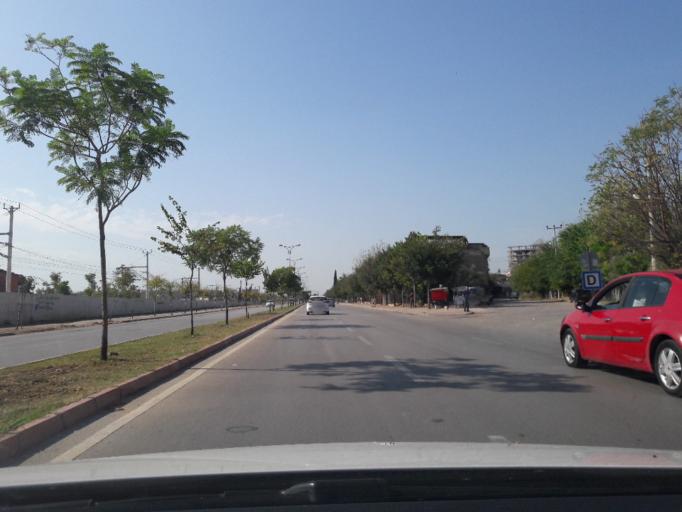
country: TR
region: Adana
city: Seyhan
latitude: 37.0015
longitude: 35.3084
